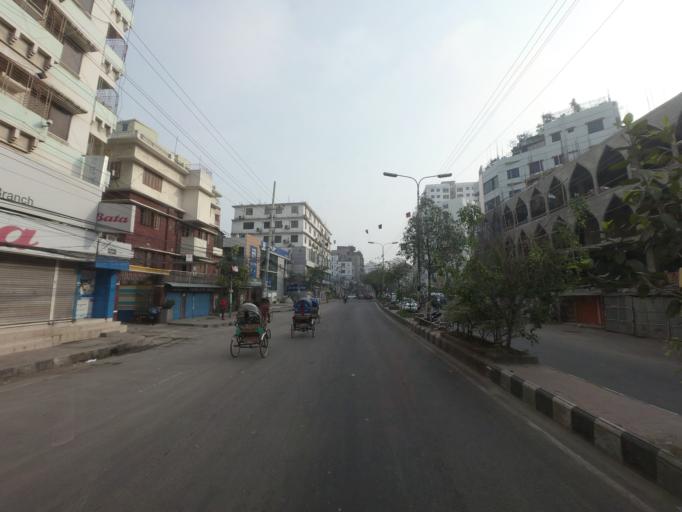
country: BD
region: Dhaka
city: Azimpur
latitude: 23.7699
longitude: 90.3588
